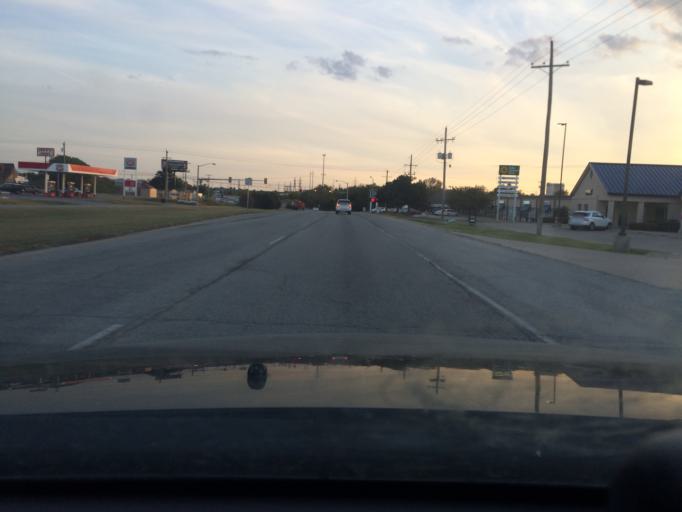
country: US
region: Oklahoma
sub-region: Rogers County
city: Catoosa
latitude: 36.1785
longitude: -95.7501
